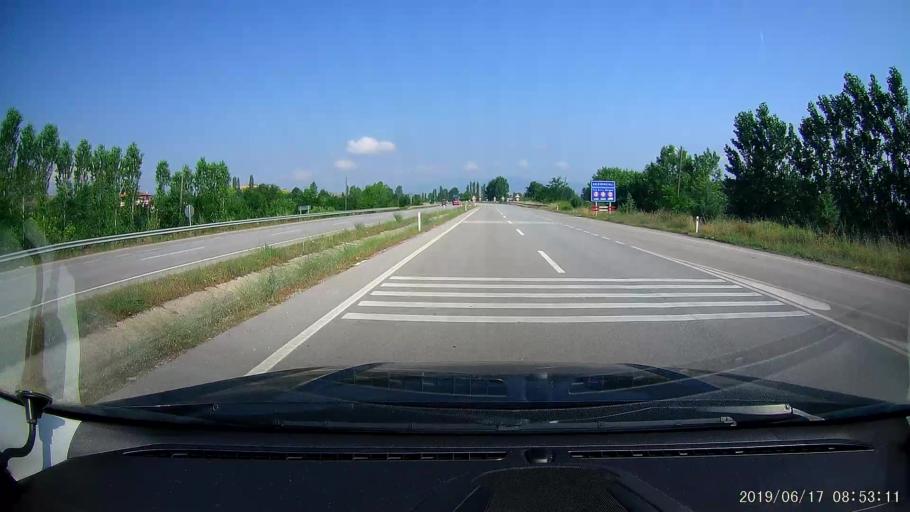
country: TR
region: Tokat
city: Erbaa
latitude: 40.7071
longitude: 36.4855
